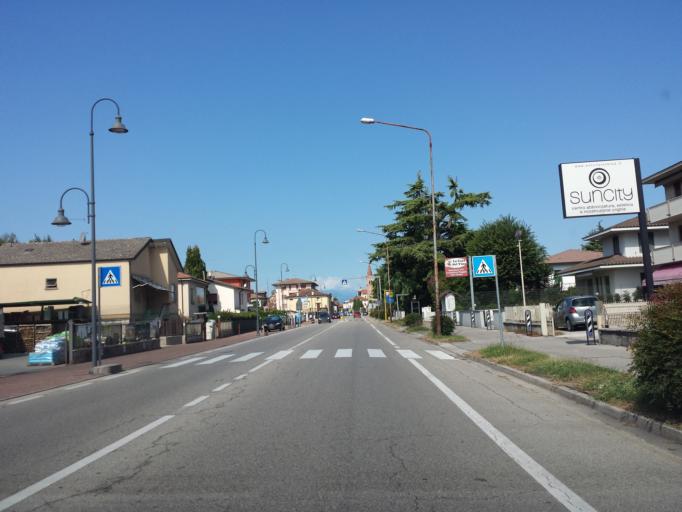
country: IT
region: Veneto
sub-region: Provincia di Vicenza
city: Torri di Quartesolo
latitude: 45.5172
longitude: 11.6205
